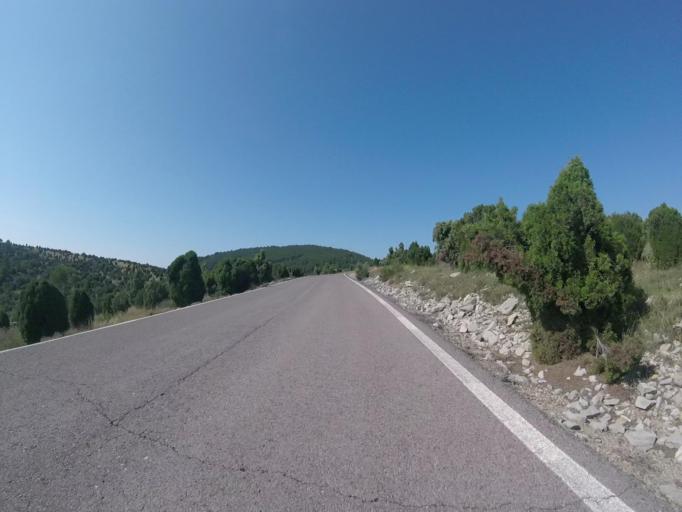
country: ES
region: Valencia
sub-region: Provincia de Castello
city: Benafigos
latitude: 40.2797
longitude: -0.2395
